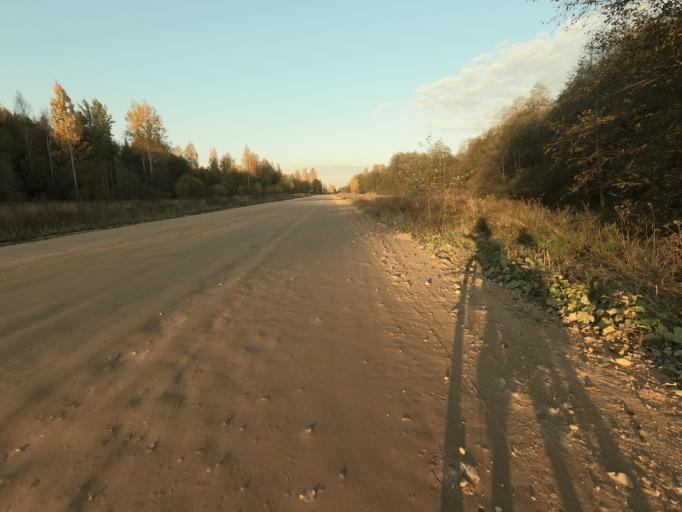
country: RU
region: Leningrad
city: Lyuban'
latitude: 59.0173
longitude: 31.0869
